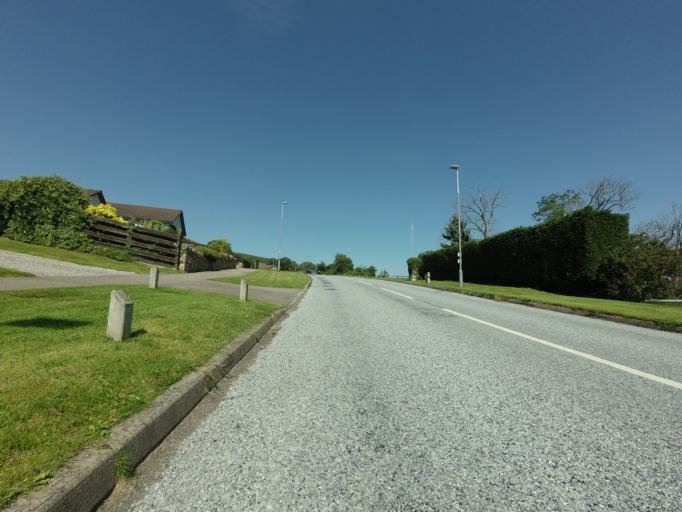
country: GB
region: Scotland
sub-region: Highland
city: Dingwall
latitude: 57.6091
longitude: -4.4202
